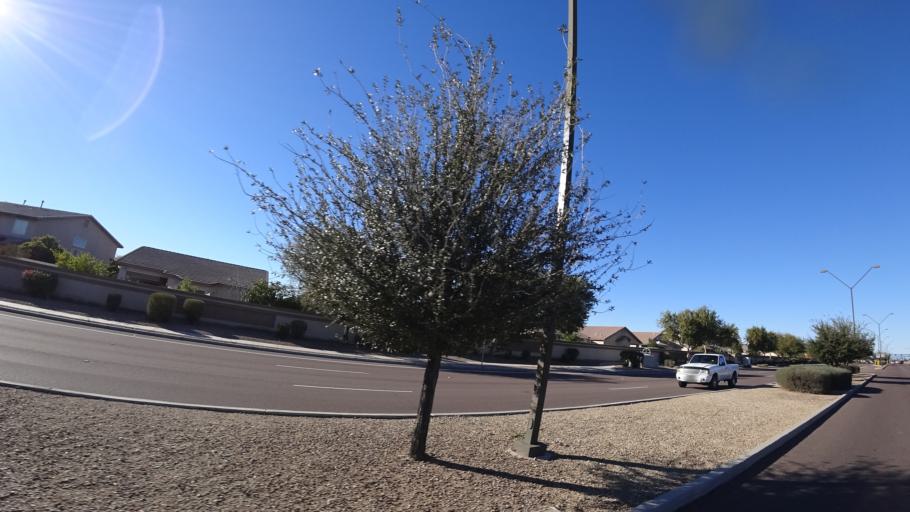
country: US
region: Arizona
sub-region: Maricopa County
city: Avondale
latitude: 33.4422
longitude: -112.3064
